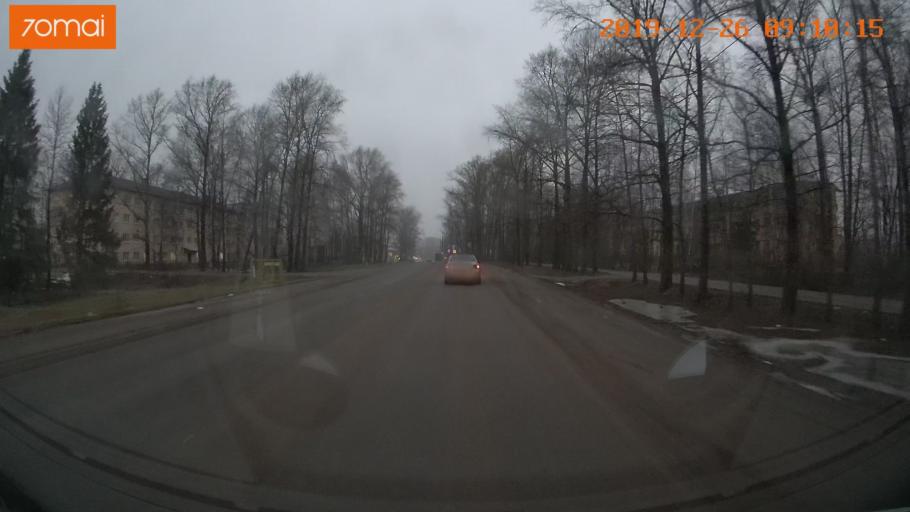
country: RU
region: Vologda
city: Gryazovets
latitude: 58.8698
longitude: 40.2528
